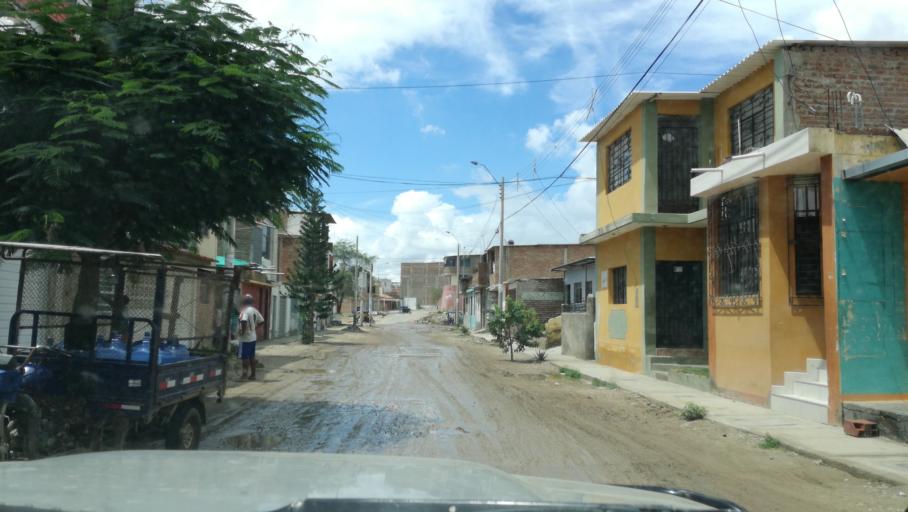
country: PE
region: Piura
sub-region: Provincia de Piura
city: Piura
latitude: -5.1769
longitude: -80.6461
